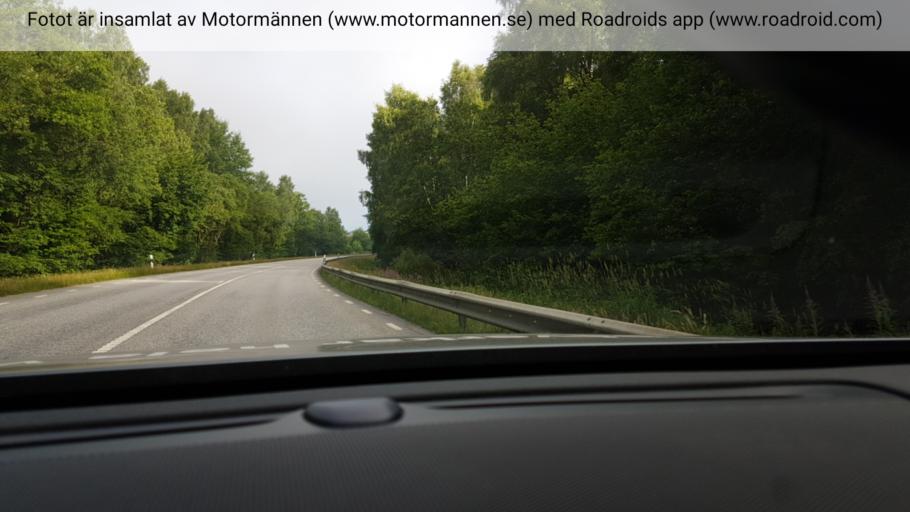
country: SE
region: Skane
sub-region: Hassleholms Kommun
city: Bjarnum
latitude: 56.2729
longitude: 13.7153
